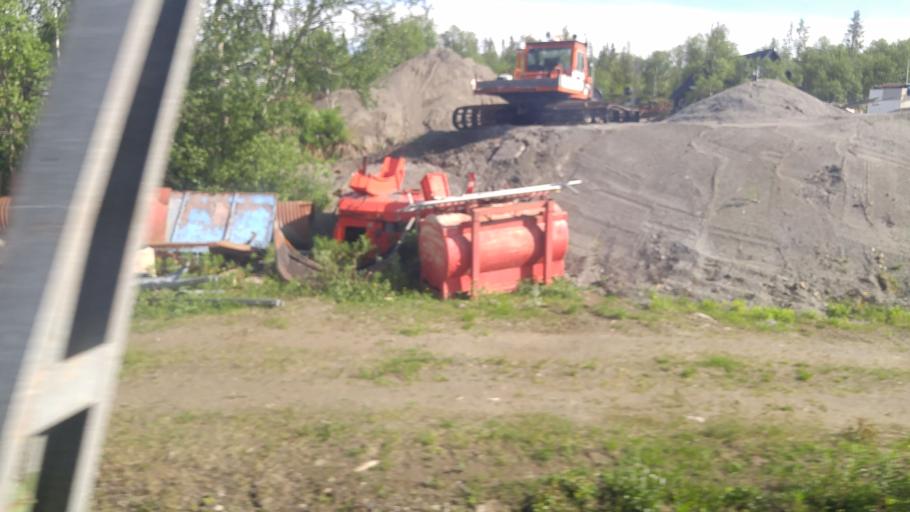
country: NO
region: Nord-Trondelag
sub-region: Meraker
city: Meraker
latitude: 63.3138
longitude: 12.1105
